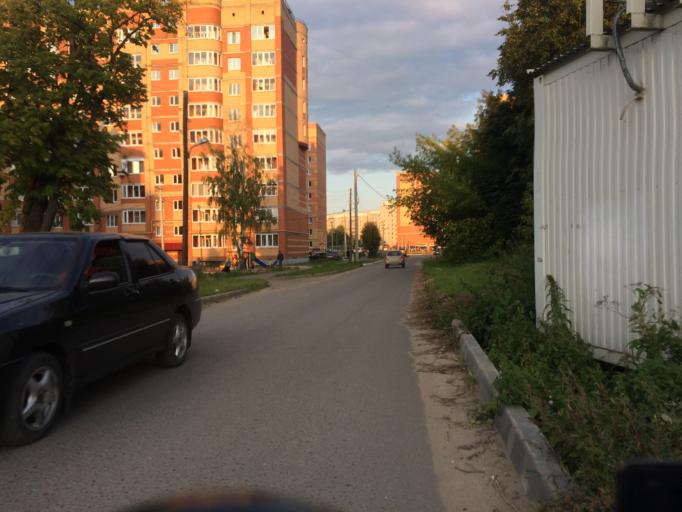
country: RU
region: Mariy-El
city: Medvedevo
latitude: 56.6443
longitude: 47.8456
